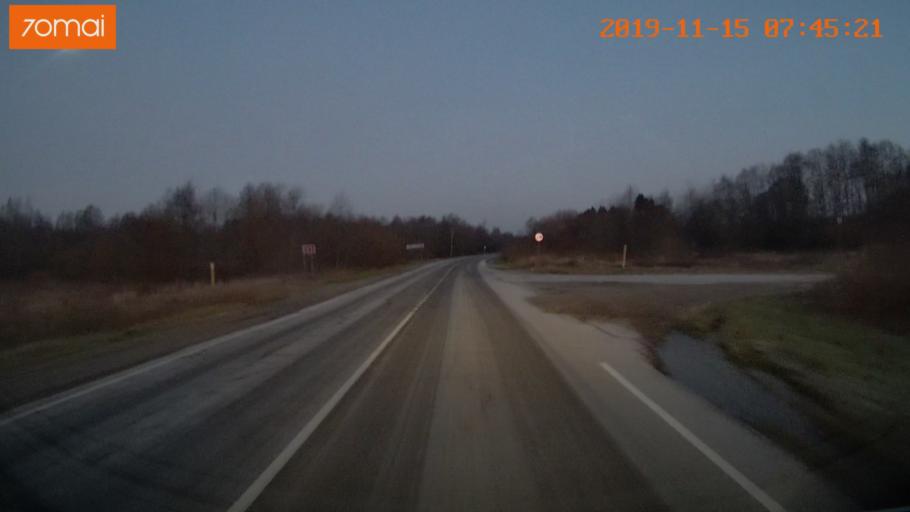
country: RU
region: Vologda
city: Sheksna
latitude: 58.8222
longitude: 38.3002
